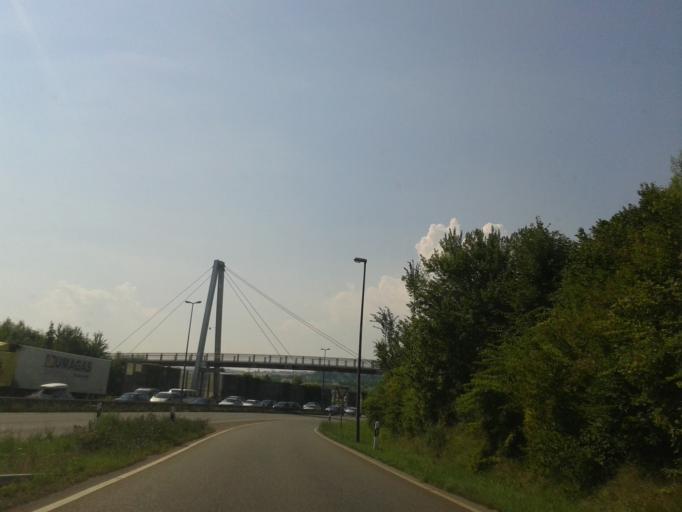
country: DE
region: Saxony
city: Bannewitz
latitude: 51.0183
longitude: 13.7291
